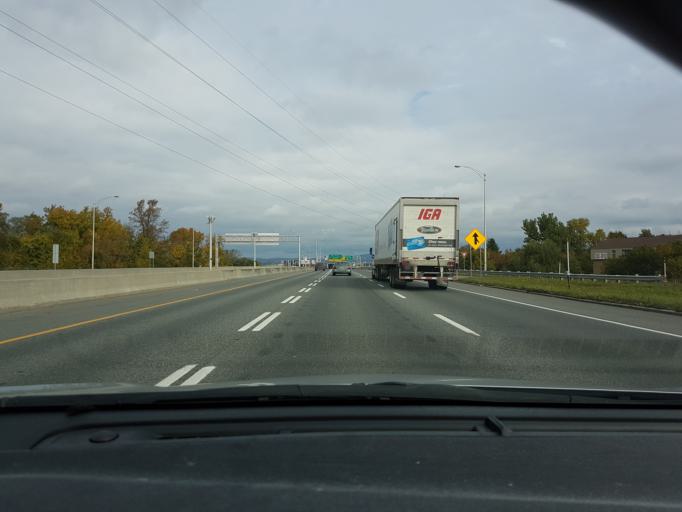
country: CA
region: Quebec
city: L'Ancienne-Lorette
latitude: 46.8087
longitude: -71.2896
